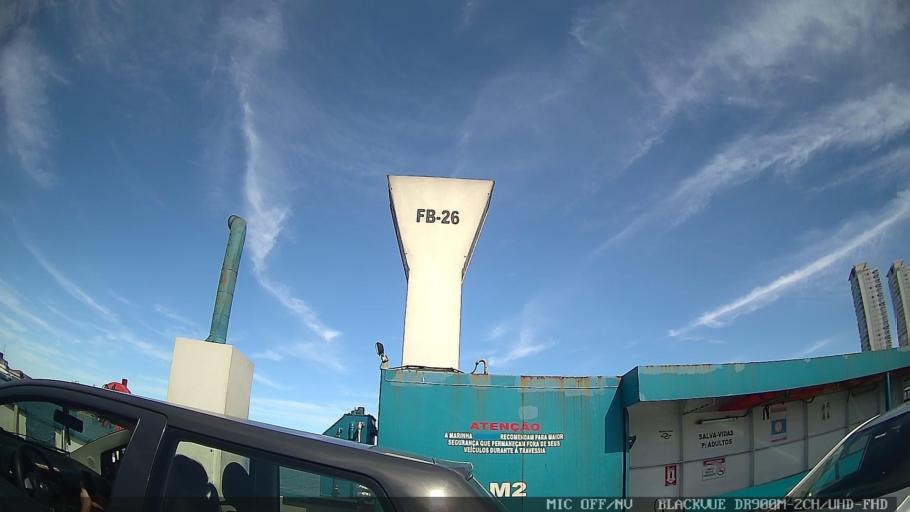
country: BR
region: Sao Paulo
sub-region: Guaruja
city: Guaruja
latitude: -23.9885
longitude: -46.2920
